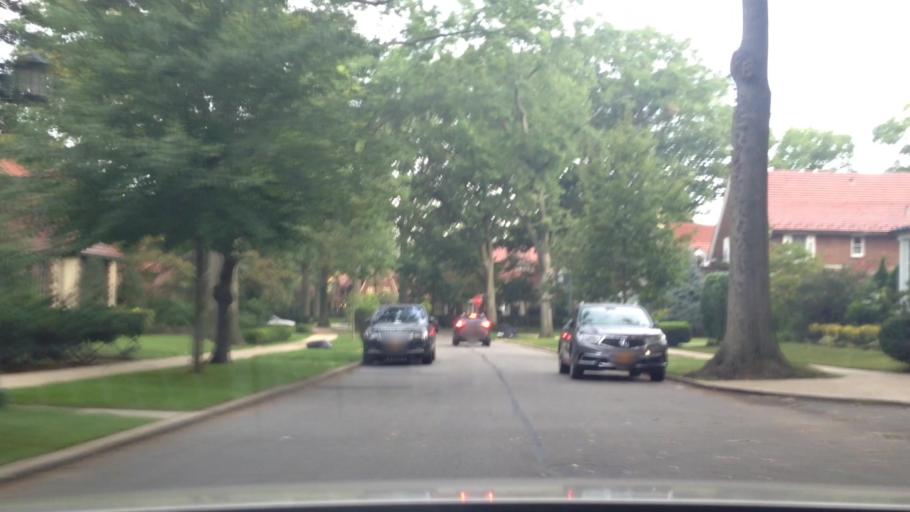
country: US
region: New York
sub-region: Queens County
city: Borough of Queens
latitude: 40.7120
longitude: -73.8407
